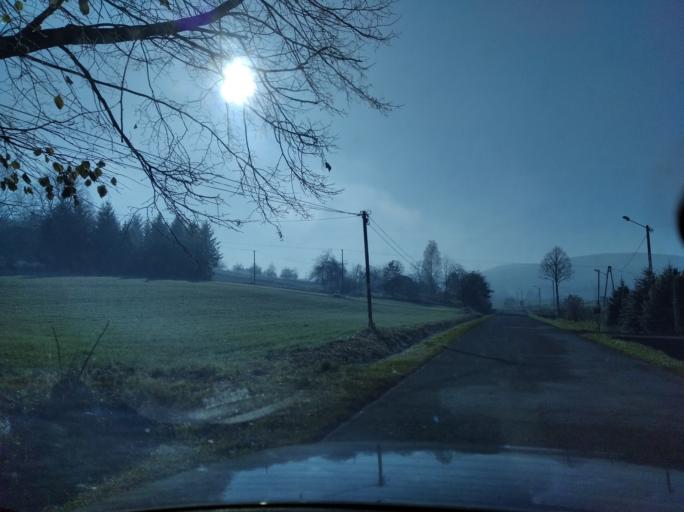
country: PL
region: Subcarpathian Voivodeship
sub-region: Powiat strzyzowski
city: Wysoka Strzyzowska
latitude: 49.8512
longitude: 21.7013
